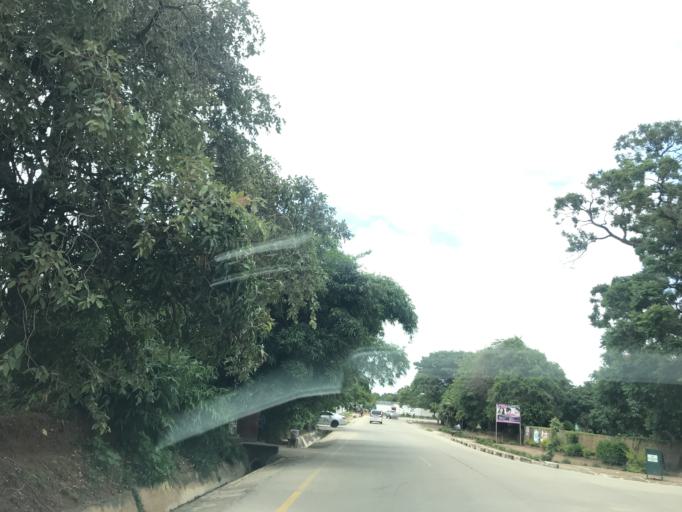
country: ZM
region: Lusaka
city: Lusaka
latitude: -15.4224
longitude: 28.3019
